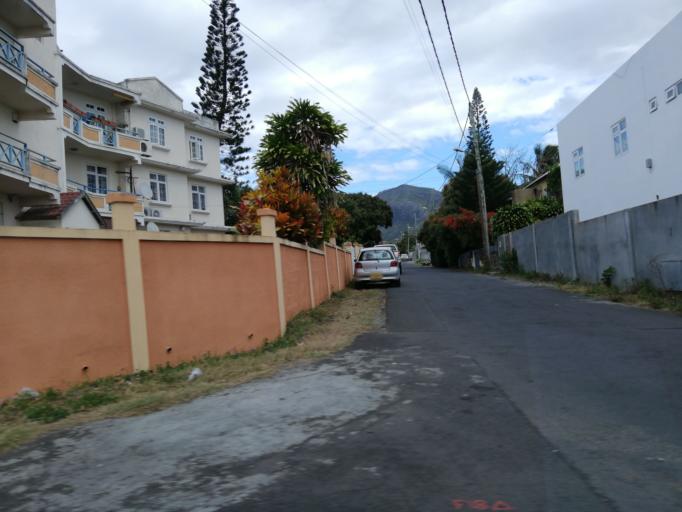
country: MU
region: Black River
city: Gros Cailloux
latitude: -20.2348
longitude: 57.4554
